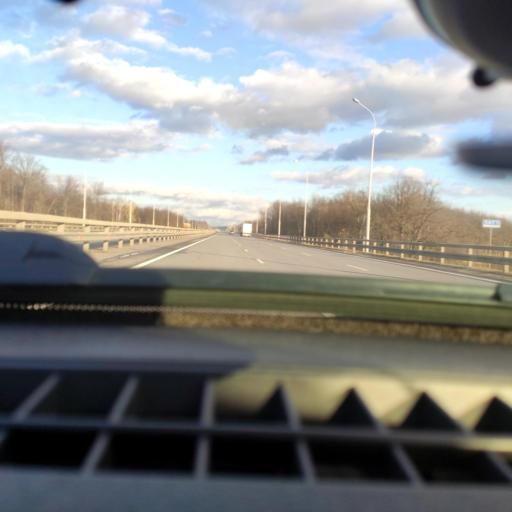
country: RU
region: Bashkortostan
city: Ufa
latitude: 54.6472
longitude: 56.0259
